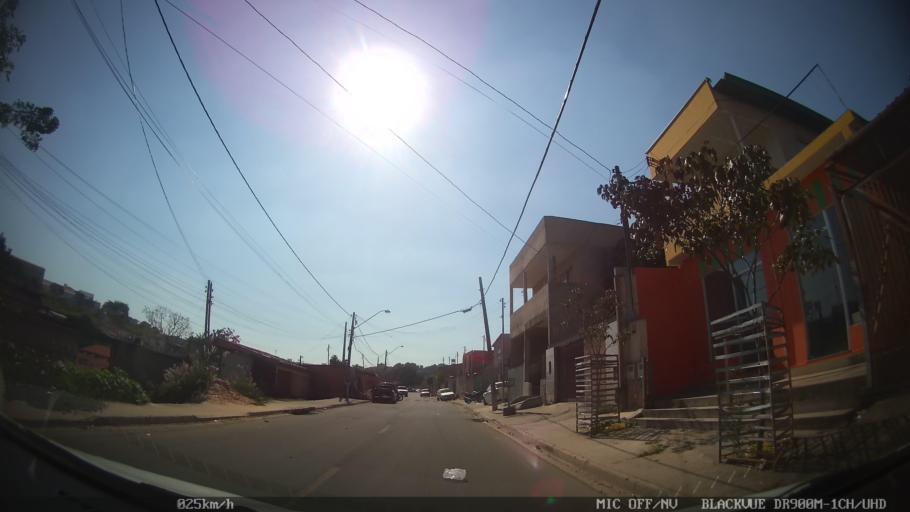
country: BR
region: Sao Paulo
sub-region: Campinas
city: Campinas
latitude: -22.9444
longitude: -47.0841
